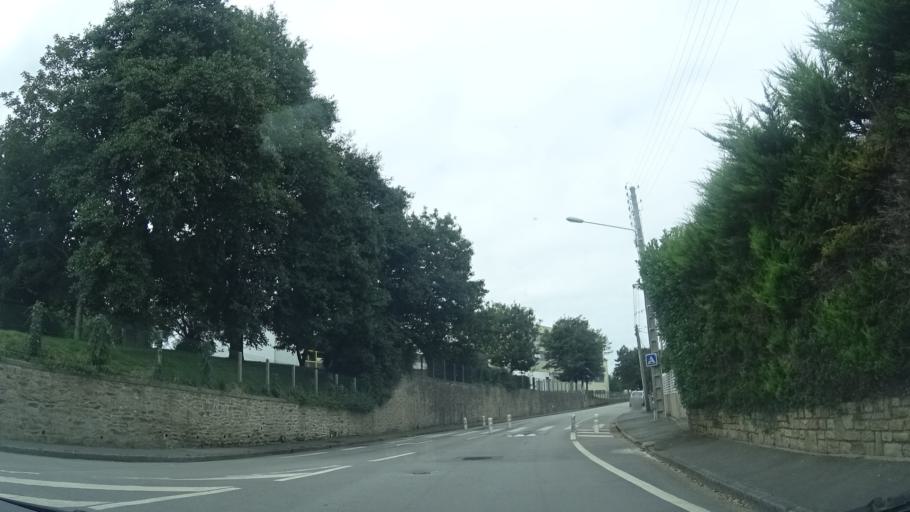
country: FR
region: Brittany
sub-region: Departement du Finistere
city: Brest
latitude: 48.4025
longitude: -4.4566
